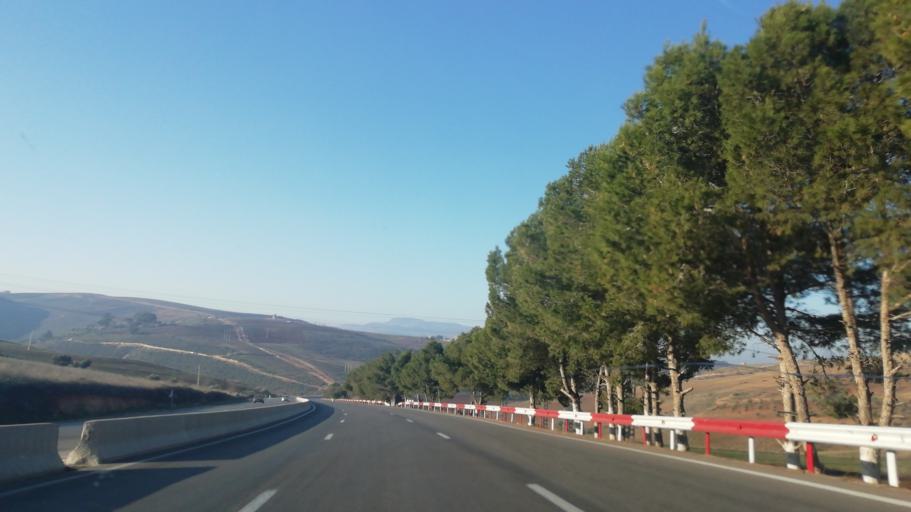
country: MA
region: Oriental
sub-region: Berkane-Taourirt
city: Ahfir
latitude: 34.9601
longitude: -1.9975
